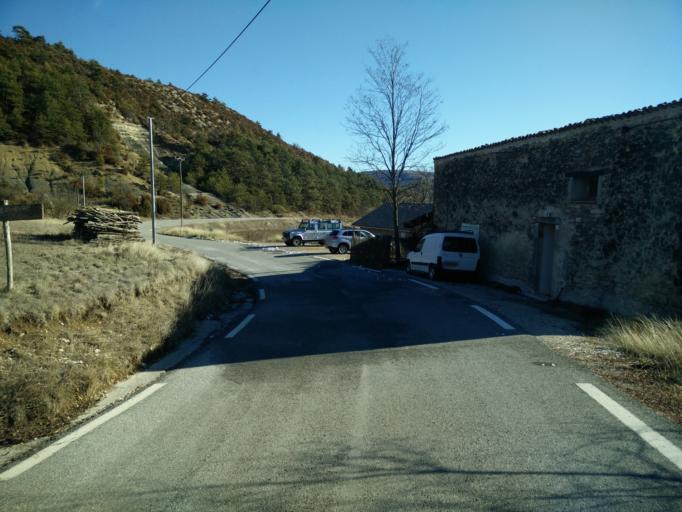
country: FR
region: Provence-Alpes-Cote d'Azur
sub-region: Departement des Alpes-de-Haute-Provence
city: Castellane
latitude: 43.7558
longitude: 6.4374
